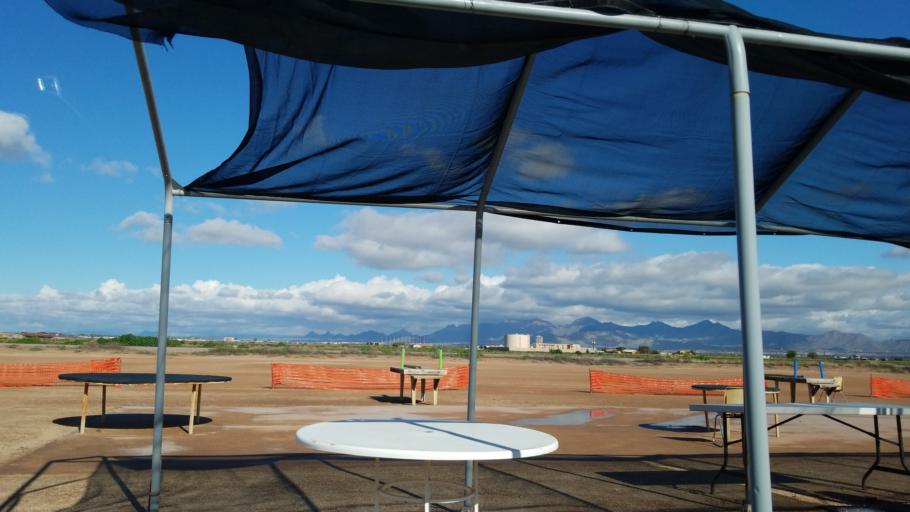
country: US
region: Arizona
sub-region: Maricopa County
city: Scottsdale
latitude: 33.5161
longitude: -111.8805
